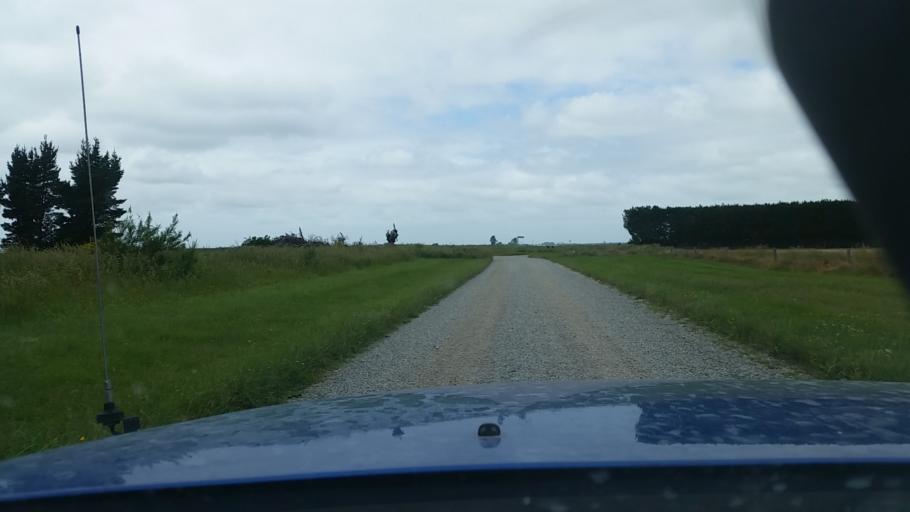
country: NZ
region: Canterbury
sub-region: Ashburton District
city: Tinwald
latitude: -44.0426
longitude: 171.4981
